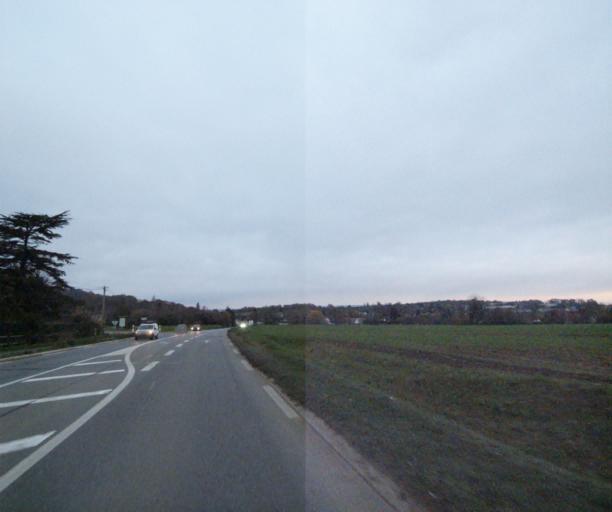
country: FR
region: Ile-de-France
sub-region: Departement des Yvelines
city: Orgeval
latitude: 48.9368
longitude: 1.9759
